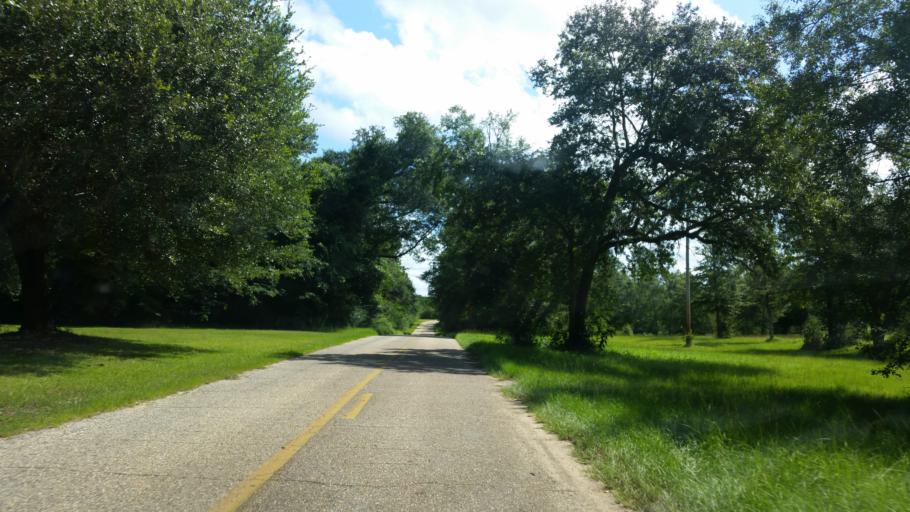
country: US
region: Florida
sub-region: Santa Rosa County
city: Point Baker
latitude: 30.7153
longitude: -86.9222
